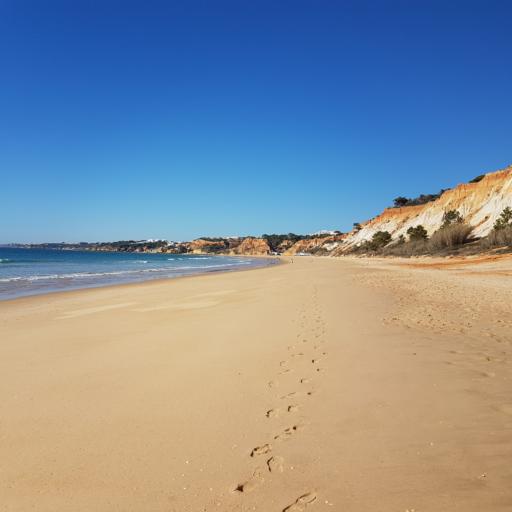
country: PT
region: Faro
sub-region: Loule
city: Boliqueime
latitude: 37.0877
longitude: -8.1722
